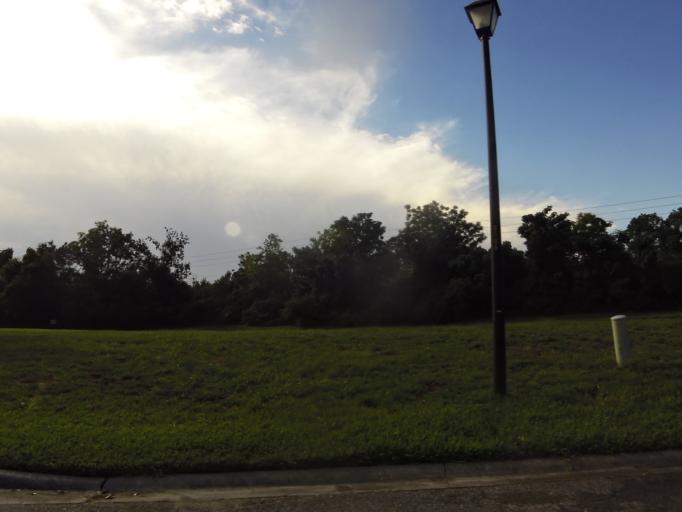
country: US
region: Florida
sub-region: Saint Johns County
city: Ponte Vedra Beach
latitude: 30.2147
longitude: -81.5329
